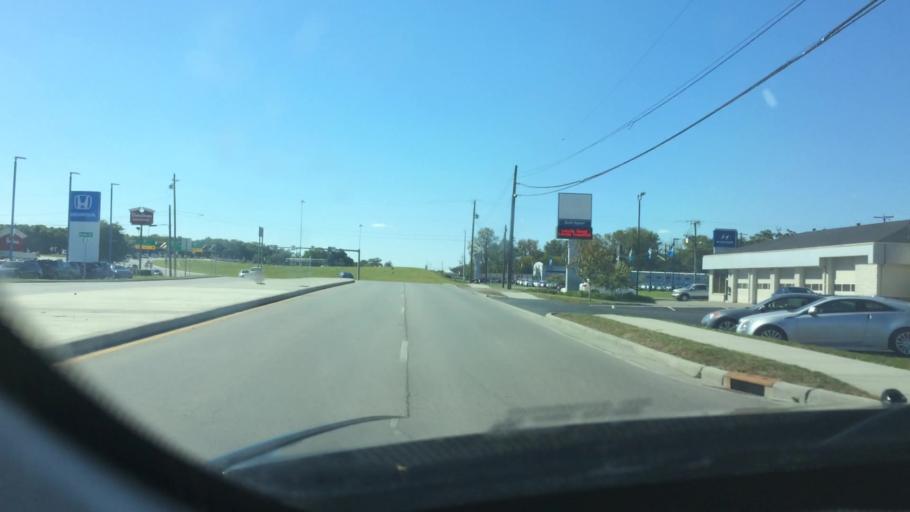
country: US
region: Ohio
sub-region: Lucas County
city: Ottawa Hills
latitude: 41.6760
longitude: -83.6889
